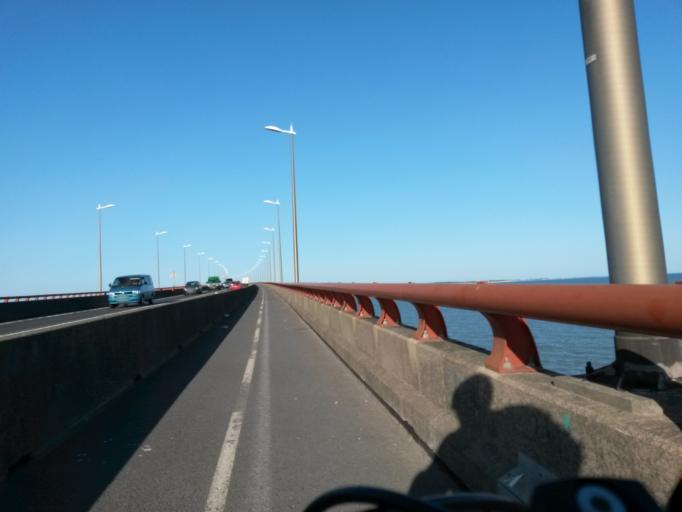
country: FR
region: Poitou-Charentes
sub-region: Departement de la Charente-Maritime
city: Rivedoux-Plage
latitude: 46.1756
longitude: -1.2233
